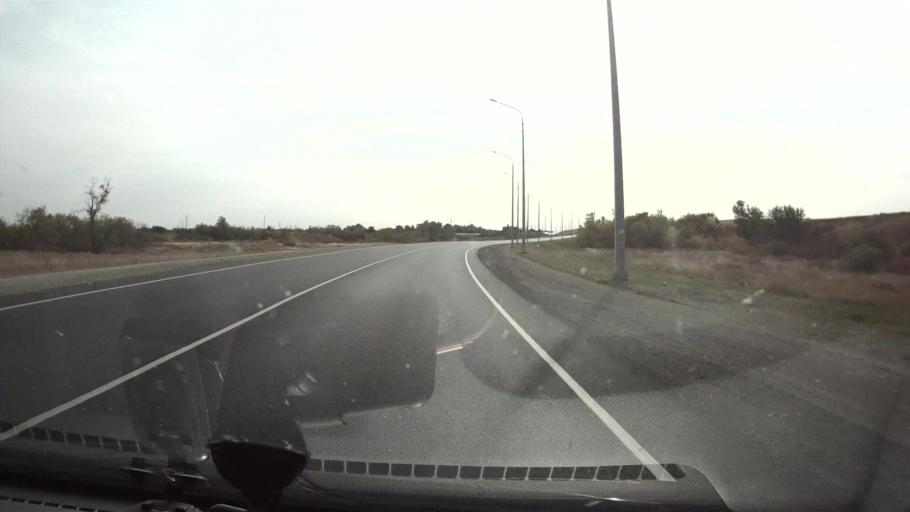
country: RU
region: Saratov
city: Sennoy
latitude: 52.0903
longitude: 46.8102
